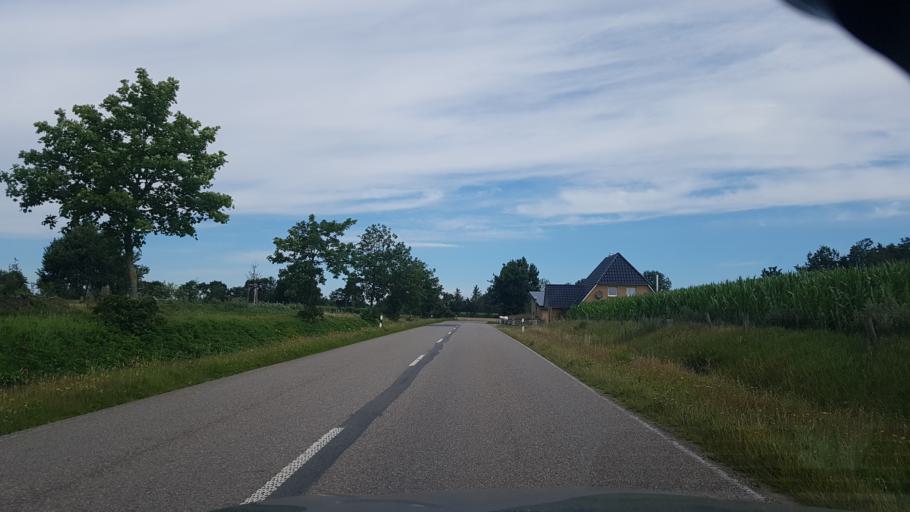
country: DE
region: Schleswig-Holstein
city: Ladelund
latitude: 54.8435
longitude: 9.0347
